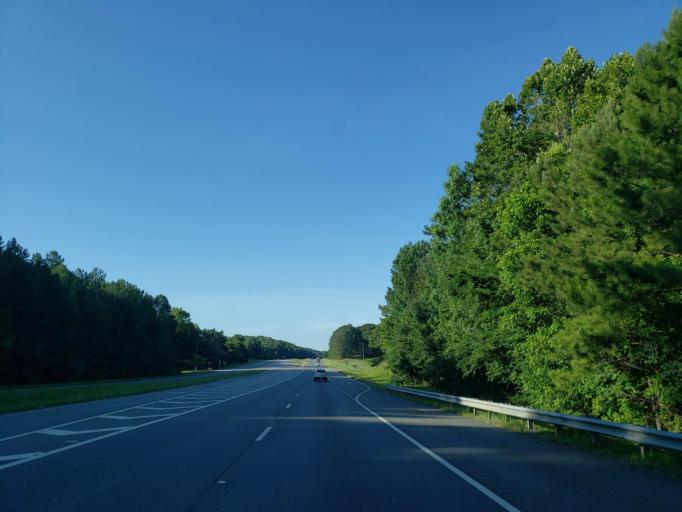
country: US
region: Georgia
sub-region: Floyd County
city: Shannon
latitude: 34.3033
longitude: -85.1147
